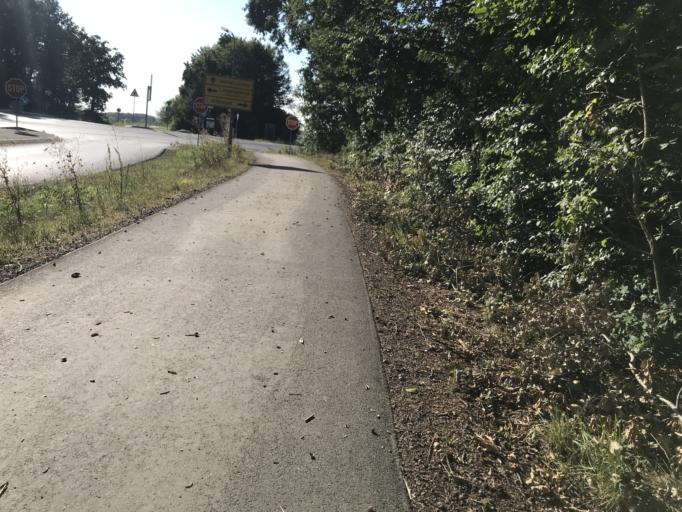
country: DE
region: Hesse
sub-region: Regierungsbezirk Darmstadt
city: Altenstadt
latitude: 50.2687
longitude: 8.9568
